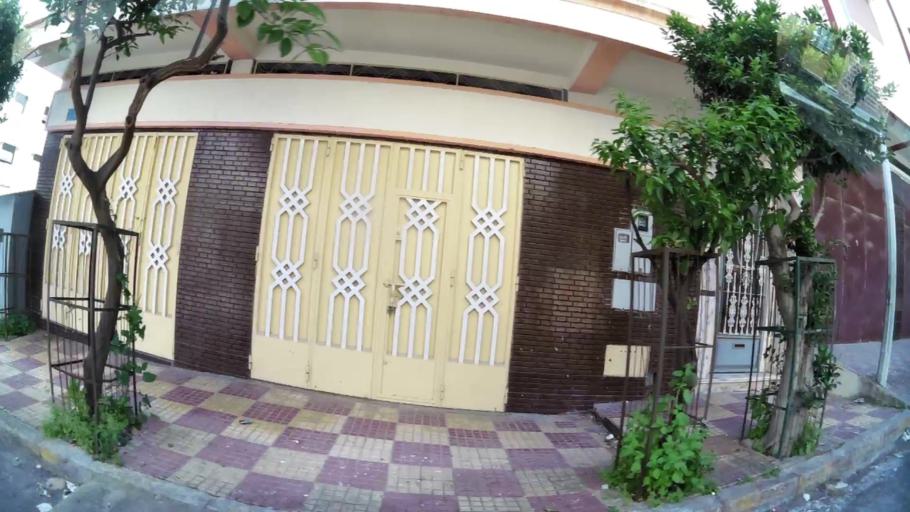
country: MA
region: Tanger-Tetouan
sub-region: Tanger-Assilah
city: Tangier
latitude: 35.7566
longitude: -5.8031
